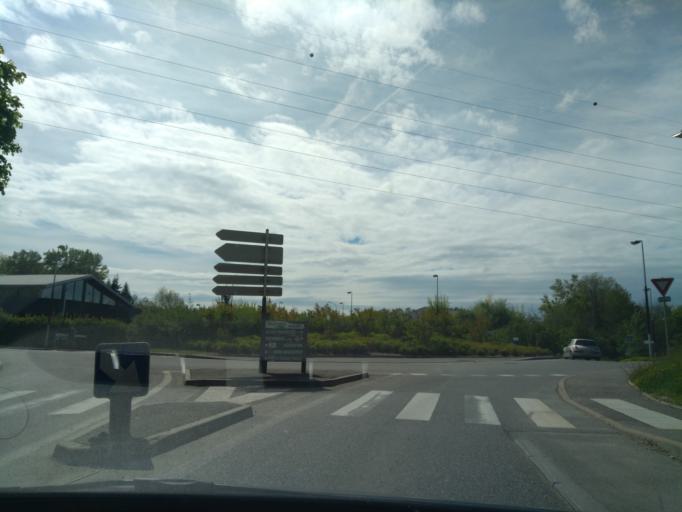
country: FR
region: Rhone-Alpes
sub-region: Departement de la Haute-Savoie
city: Seynod
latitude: 45.8901
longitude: 6.0832
